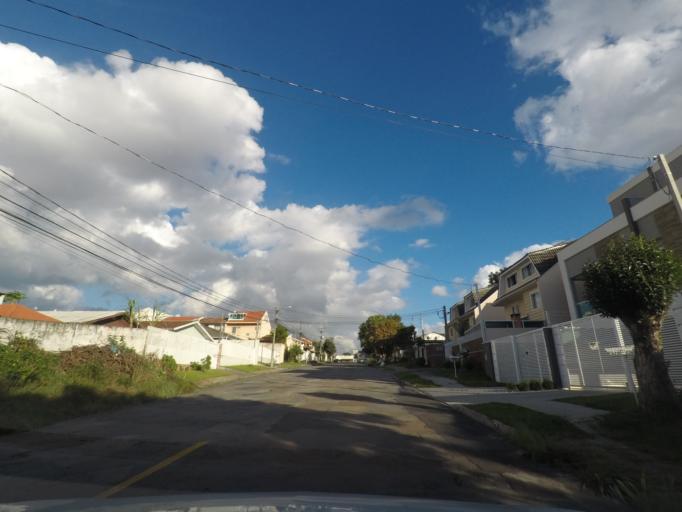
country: BR
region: Parana
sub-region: Sao Jose Dos Pinhais
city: Sao Jose dos Pinhais
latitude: -25.4992
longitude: -49.2540
